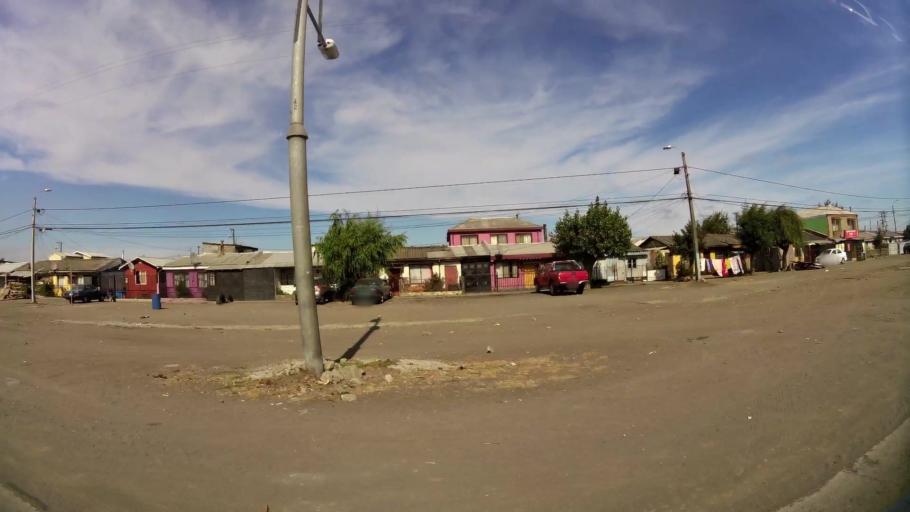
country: CL
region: Biobio
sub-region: Provincia de Concepcion
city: Talcahuano
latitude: -36.7840
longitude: -73.1112
